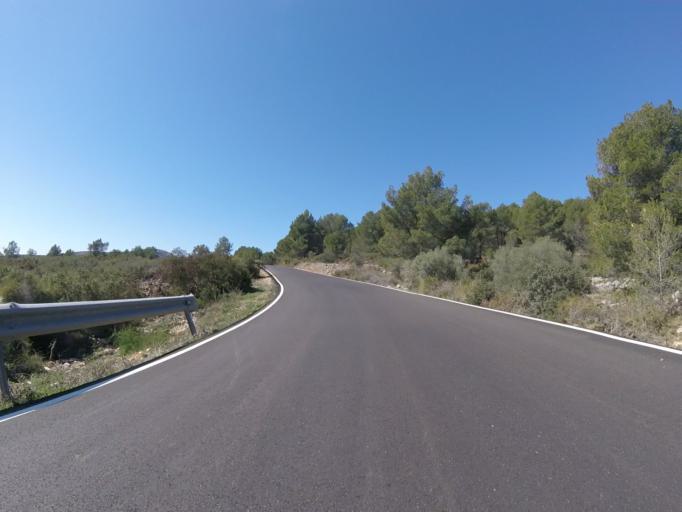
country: ES
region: Valencia
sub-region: Provincia de Castello
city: Cervera del Maestre
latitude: 40.4082
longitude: 0.2007
